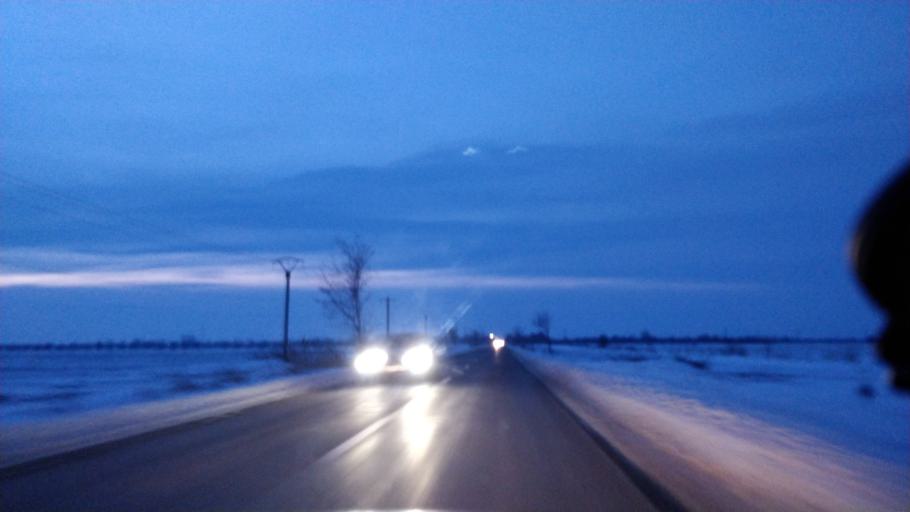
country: RO
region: Vrancea
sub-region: Comuna Vulturu
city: Vadu Rosca
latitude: 45.6046
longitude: 27.4516
